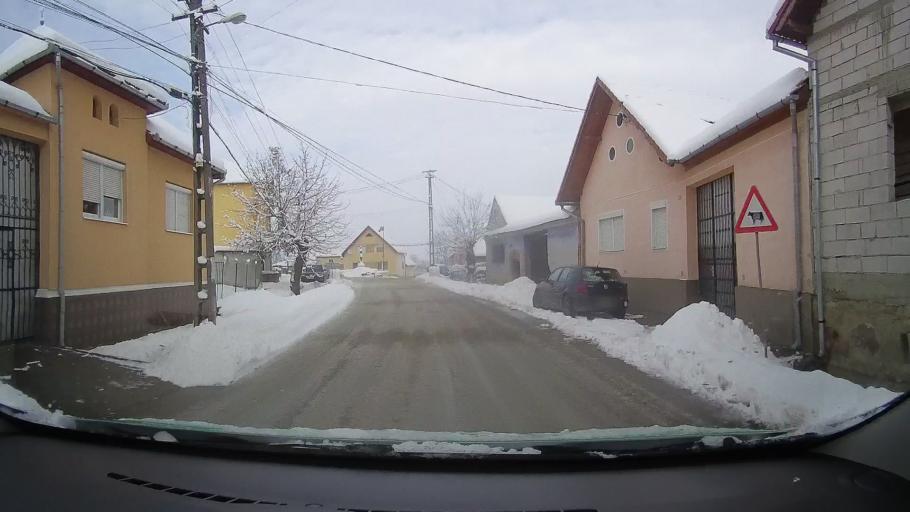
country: RO
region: Alba
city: Pianu de Sus
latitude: 45.9027
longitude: 23.4805
